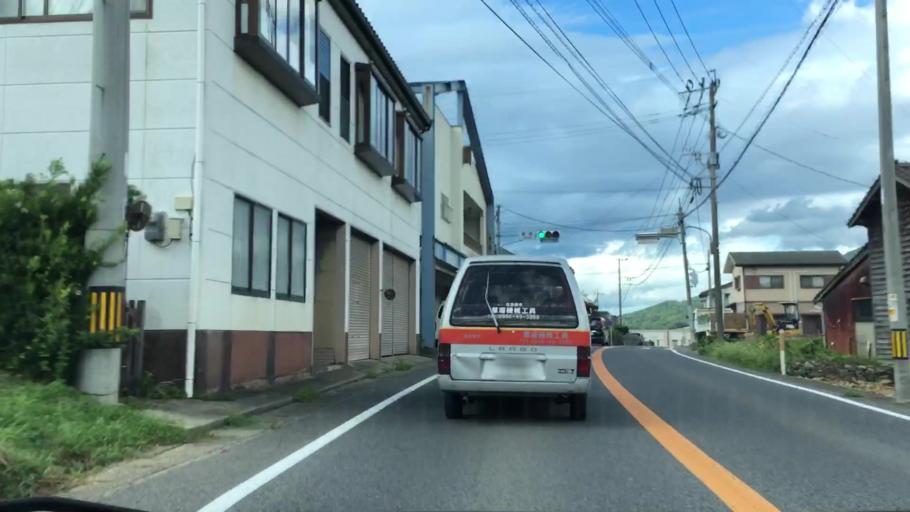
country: JP
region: Saga Prefecture
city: Imaricho-ko
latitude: 33.2048
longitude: 129.8501
